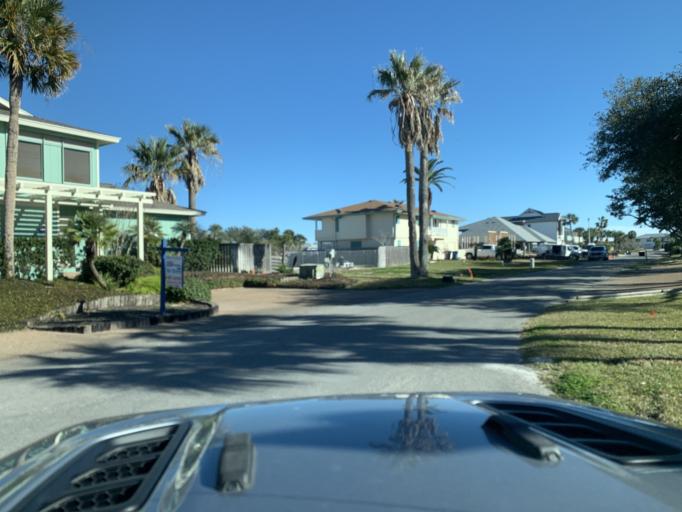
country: US
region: Texas
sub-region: Aransas County
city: Fulton
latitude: 28.0380
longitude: -97.0301
